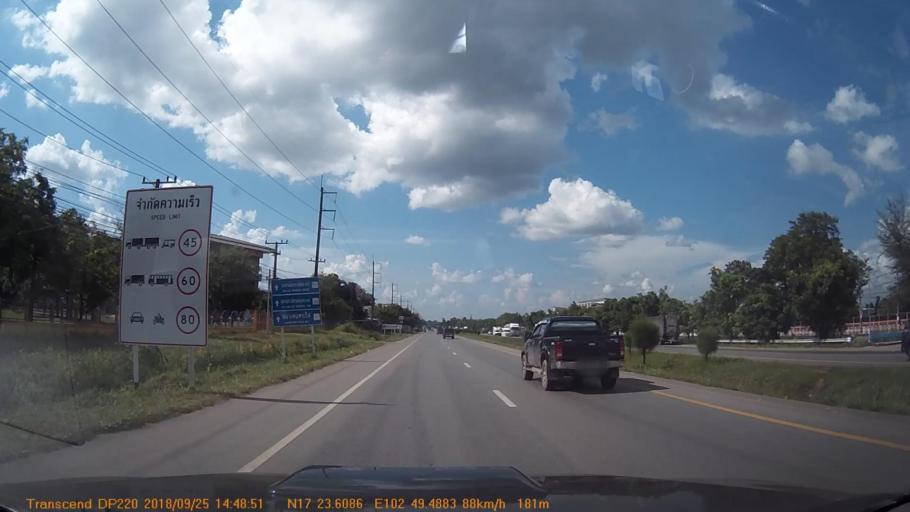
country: TH
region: Changwat Udon Thani
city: Udon Thani
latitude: 17.3940
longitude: 102.8246
